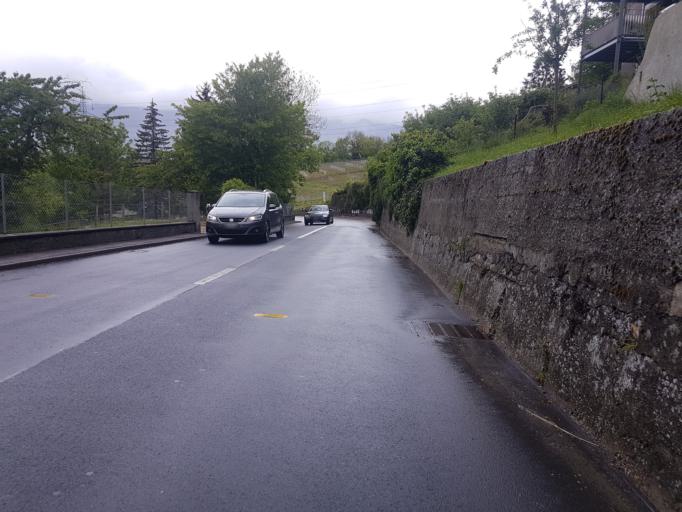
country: CH
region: Geneva
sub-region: Geneva
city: Dardagny
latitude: 46.1883
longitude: 6.0116
